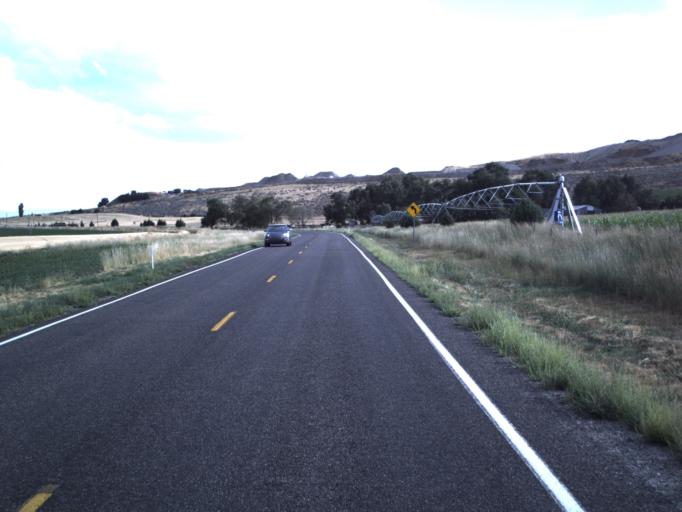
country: US
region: Utah
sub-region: Cache County
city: Benson
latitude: 41.8841
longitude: -111.9514
